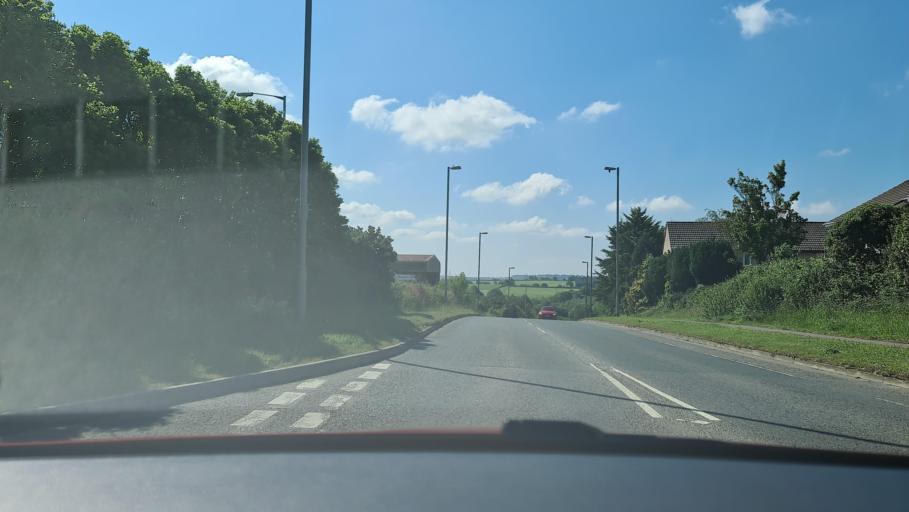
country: GB
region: England
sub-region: Cornwall
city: Liskeard
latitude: 50.4591
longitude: -4.4506
